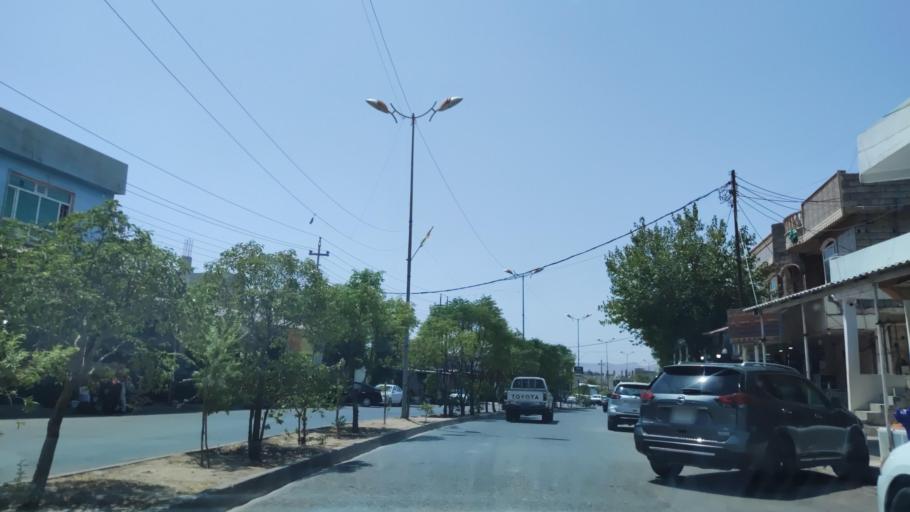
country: IQ
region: Arbil
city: Shaqlawah
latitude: 36.5514
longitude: 44.3549
